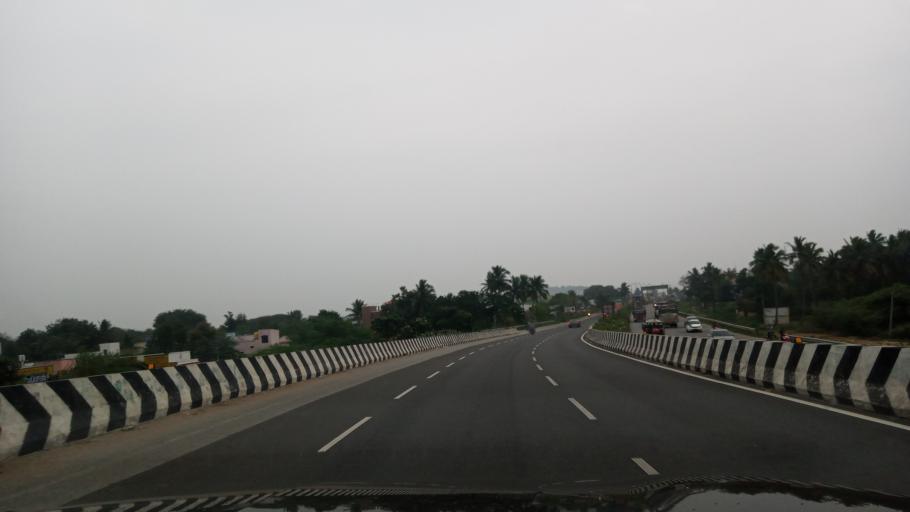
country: IN
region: Tamil Nadu
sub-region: Vellore
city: Walajapet
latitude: 12.9168
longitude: 79.3888
